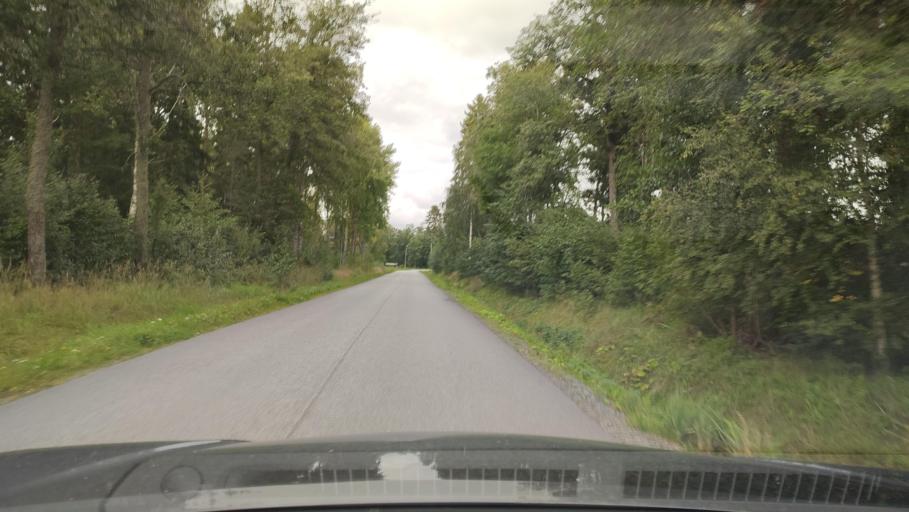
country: FI
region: Ostrobothnia
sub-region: Sydosterbotten
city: Kristinestad
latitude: 62.2621
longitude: 21.3605
